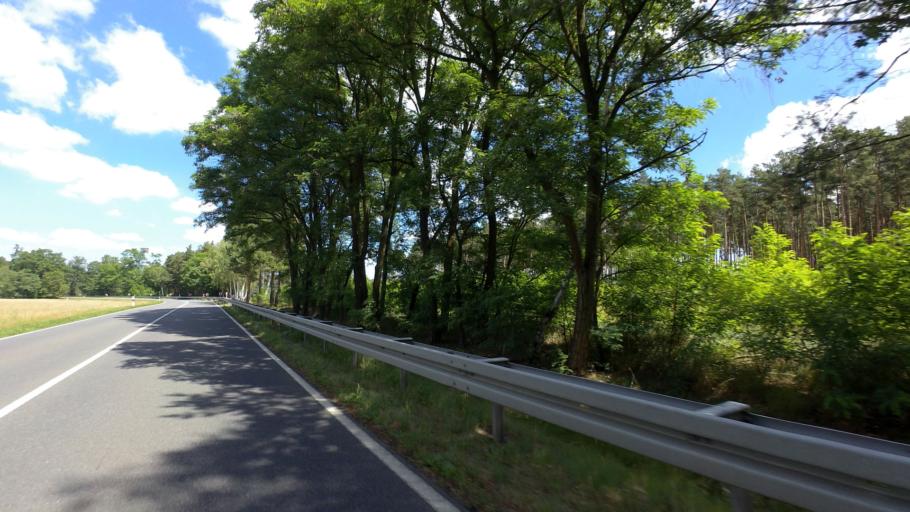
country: DE
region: Brandenburg
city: Sonnewalde
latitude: 51.7624
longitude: 13.6858
